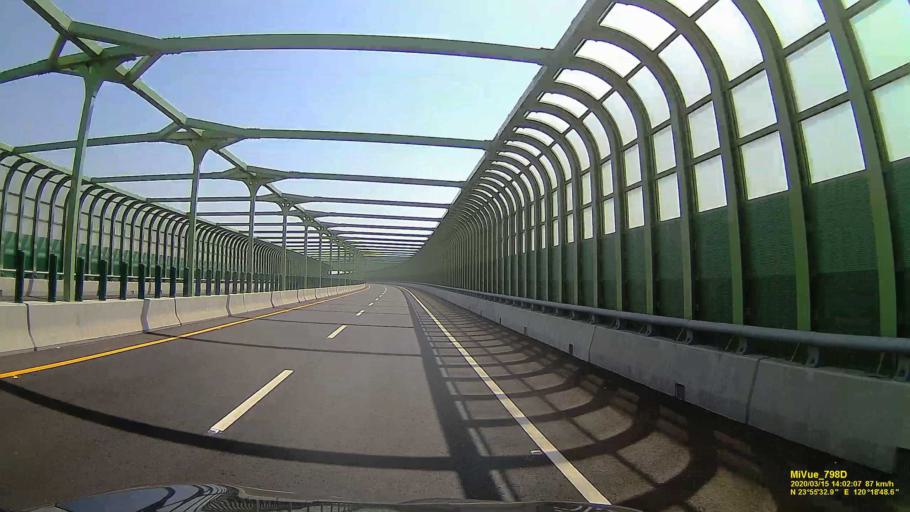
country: TW
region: Taiwan
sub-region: Changhua
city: Chang-hua
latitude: 23.9265
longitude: 120.3139
